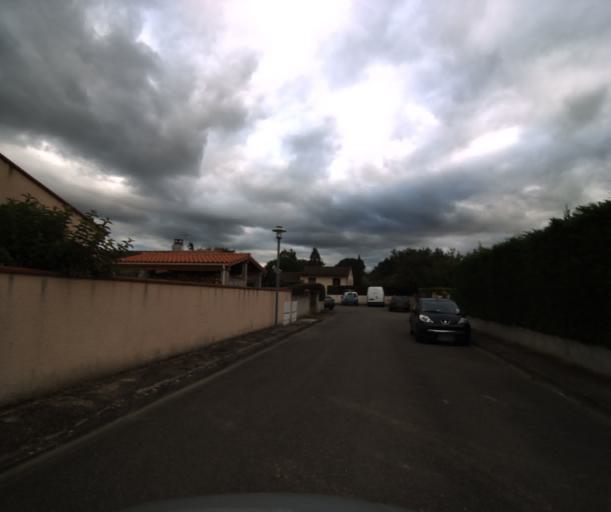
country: FR
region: Midi-Pyrenees
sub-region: Departement de la Haute-Garonne
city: Le Fauga
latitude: 43.4169
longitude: 1.3121
